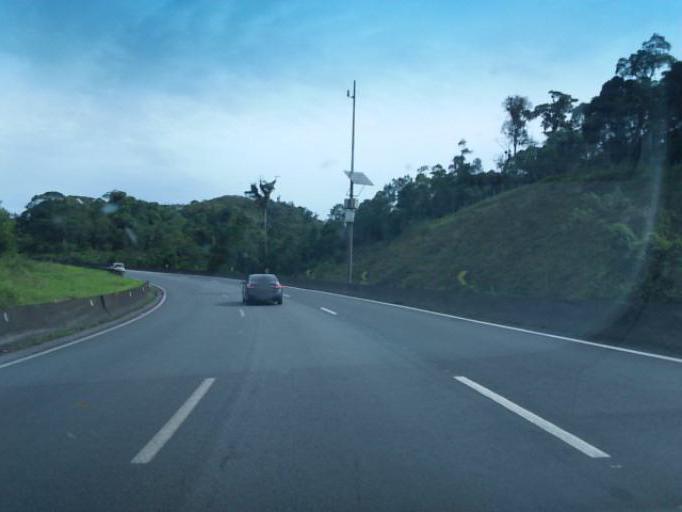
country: BR
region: Sao Paulo
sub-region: Cajati
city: Cajati
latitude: -24.9063
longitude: -48.2552
